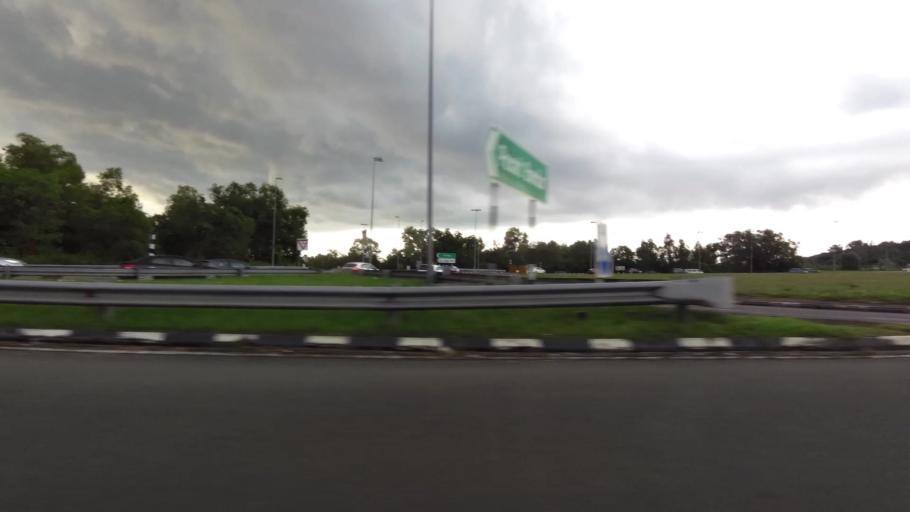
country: BN
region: Brunei and Muara
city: Bandar Seri Begawan
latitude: 4.9321
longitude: 114.9746
